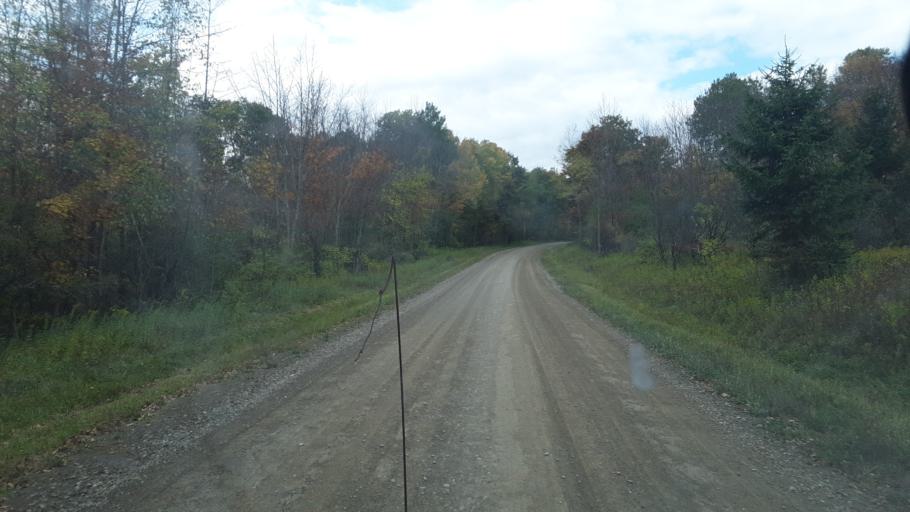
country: US
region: New York
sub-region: Allegany County
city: Alfred
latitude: 42.3805
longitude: -77.8550
